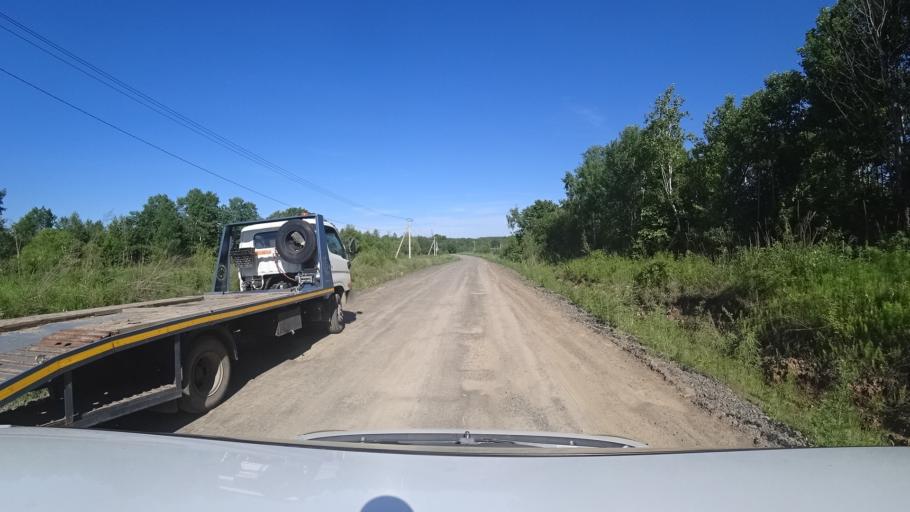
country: RU
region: Khabarovsk Krai
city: Topolevo
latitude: 48.5529
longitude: 135.1819
